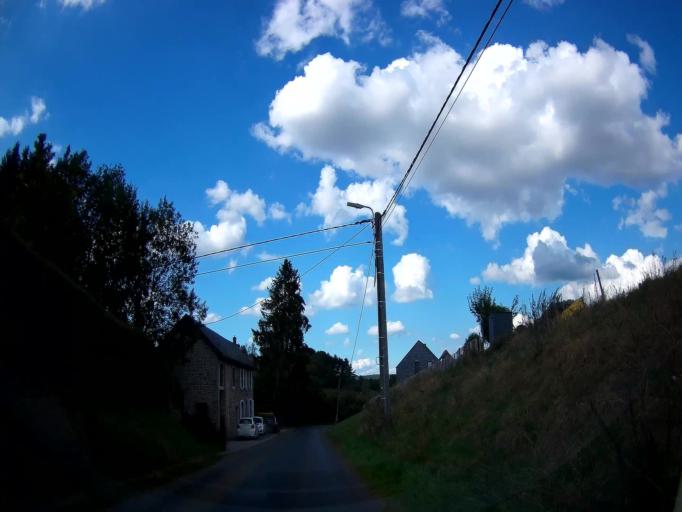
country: BE
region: Wallonia
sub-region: Province de Namur
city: Onhaye
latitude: 50.2834
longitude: 4.7915
